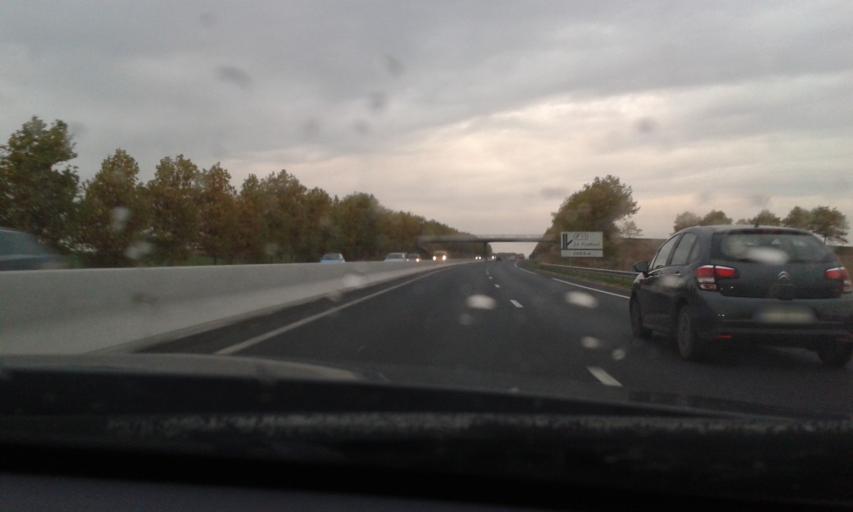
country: FR
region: Haute-Normandie
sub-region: Departement de la Seine-Maritime
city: Saint-Martin-Osmonville
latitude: 49.6269
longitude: 1.2626
